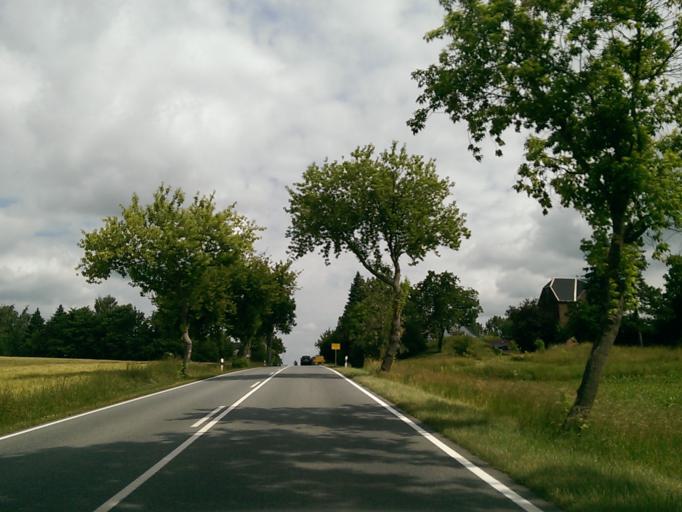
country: DE
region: Saxony
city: Mittelherwigsdorf
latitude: 50.9429
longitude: 14.7924
